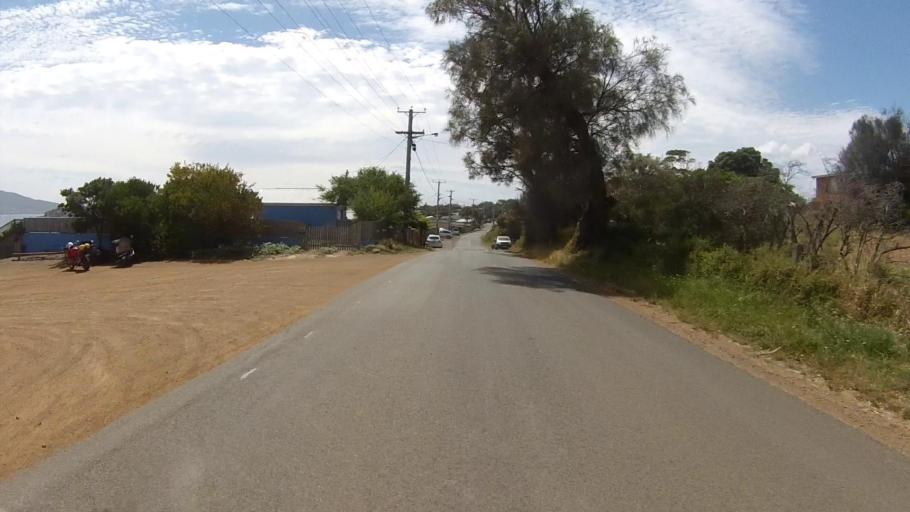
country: AU
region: Tasmania
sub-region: Kingborough
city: Taroona
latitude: -42.9926
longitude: 147.4038
